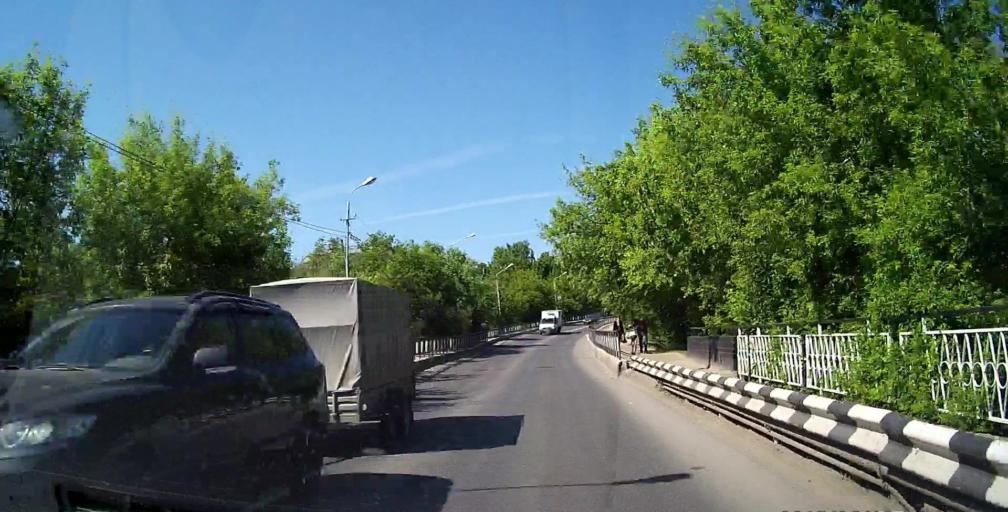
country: RU
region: Lipetsk
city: Dankov
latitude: 53.2451
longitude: 39.1444
